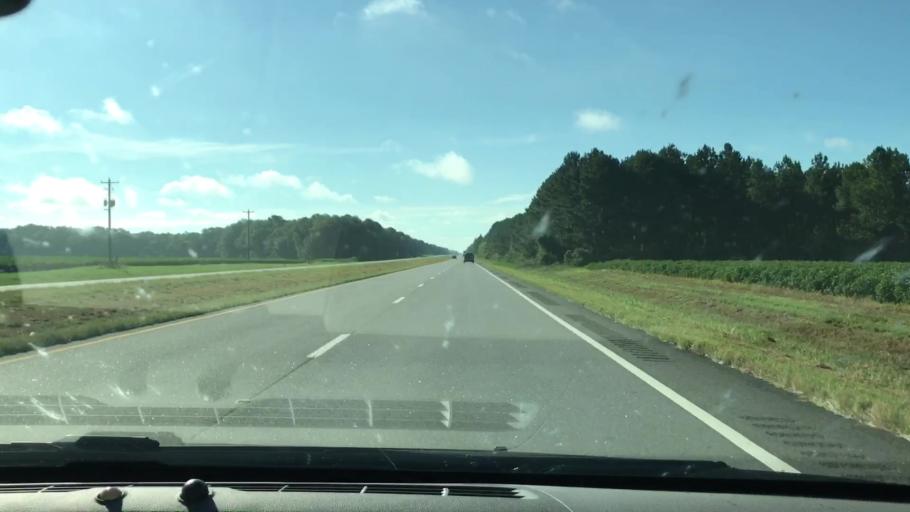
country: US
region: Georgia
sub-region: Terrell County
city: Dawson
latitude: 31.6965
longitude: -84.3193
